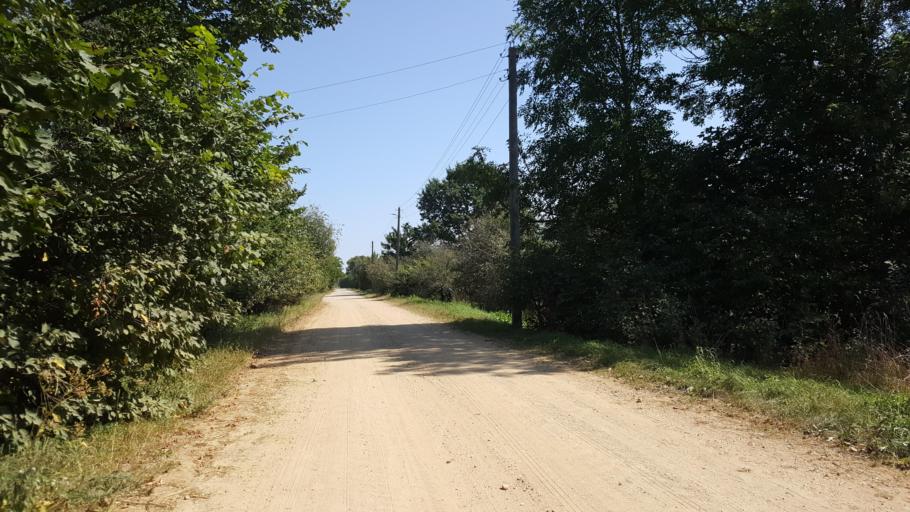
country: PL
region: Podlasie
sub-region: Powiat hajnowski
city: Czeremcha
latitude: 52.4679
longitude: 23.4579
